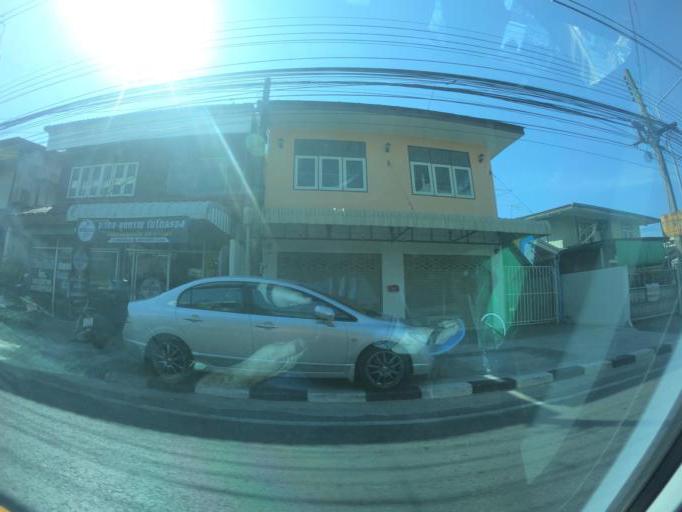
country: TH
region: Khon Kaen
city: Khon Kaen
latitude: 16.4150
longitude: 102.8341
